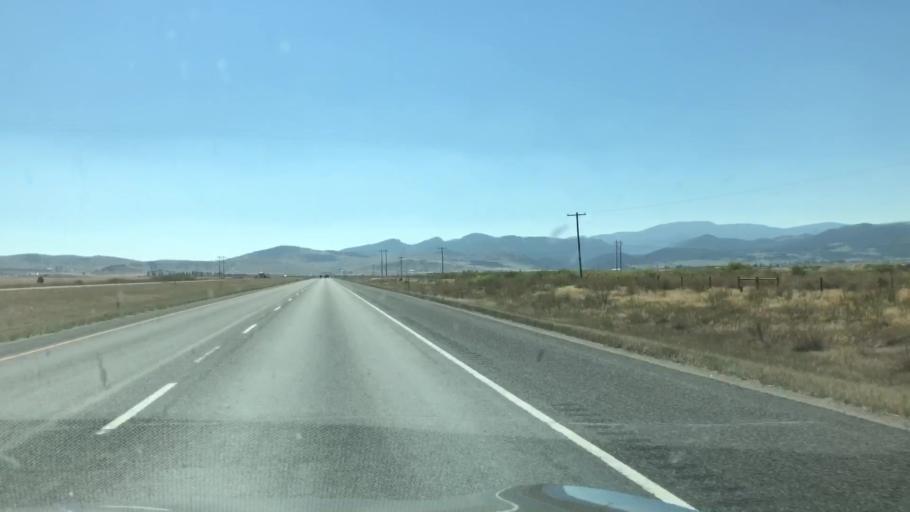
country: US
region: Montana
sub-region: Deer Lodge County
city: Warm Springs
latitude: 46.0845
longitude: -112.7892
